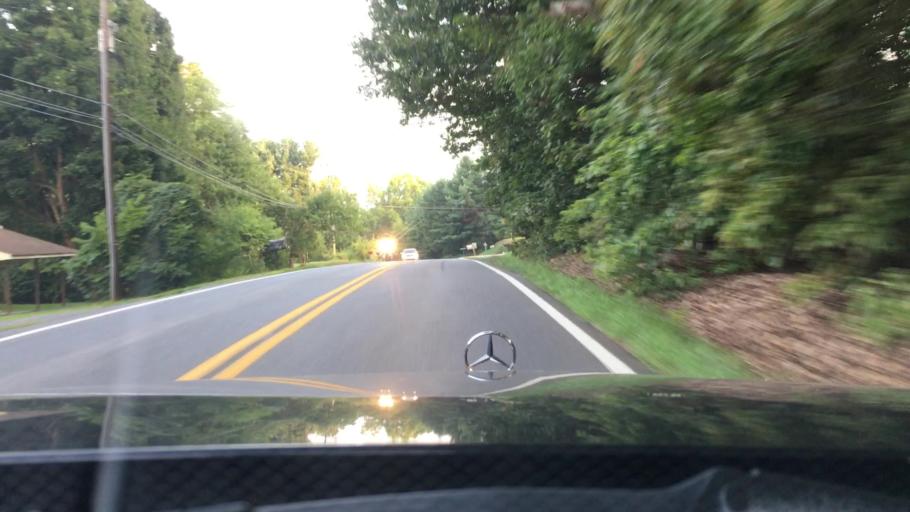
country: US
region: Virginia
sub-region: Campbell County
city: Altavista
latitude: 37.1427
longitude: -79.2955
